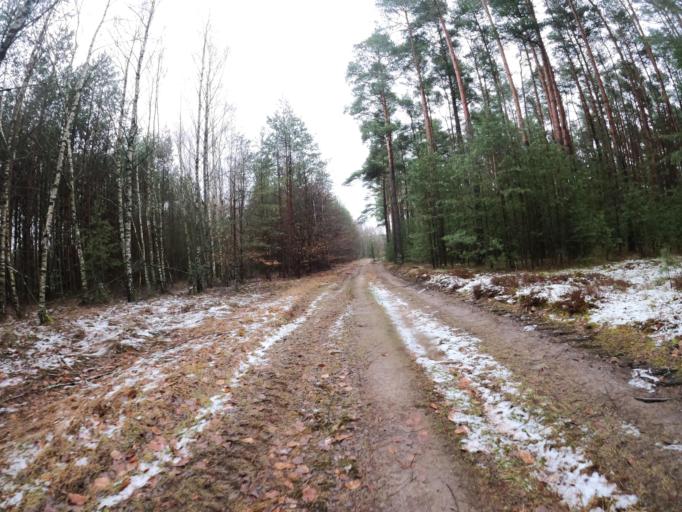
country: PL
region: Lubusz
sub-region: Powiat slubicki
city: Cybinka
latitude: 52.1958
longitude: 14.9183
